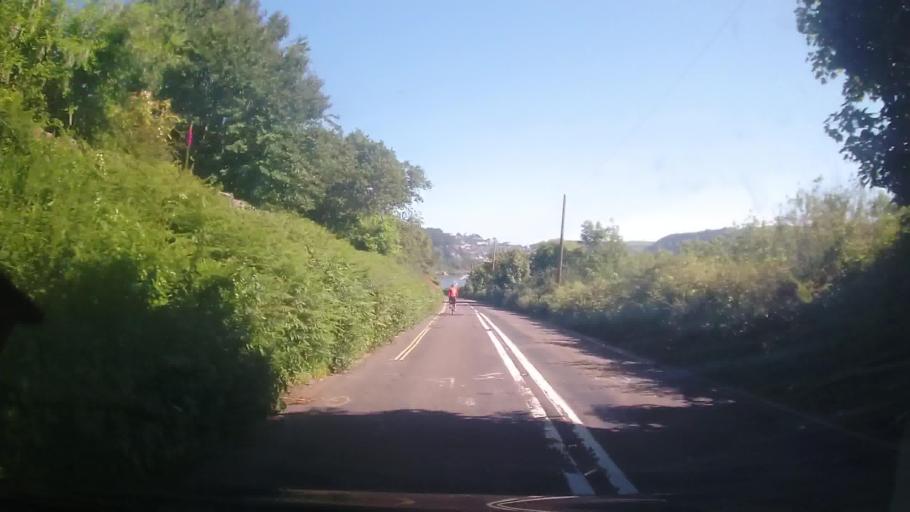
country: GB
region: England
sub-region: Devon
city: Dartmouth
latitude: 50.3626
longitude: -3.5747
